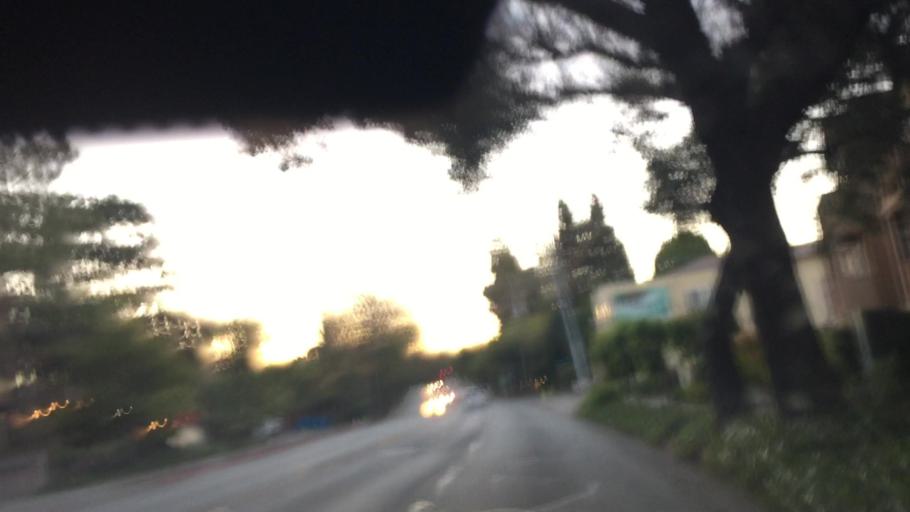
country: US
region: California
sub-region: San Mateo County
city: San Mateo
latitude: 37.5687
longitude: -122.3328
